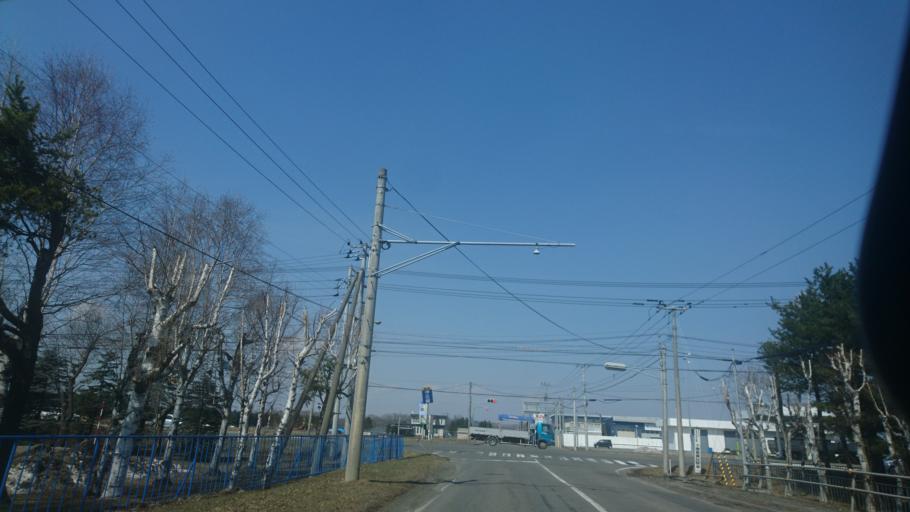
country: JP
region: Hokkaido
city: Obihiro
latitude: 42.9228
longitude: 143.0823
